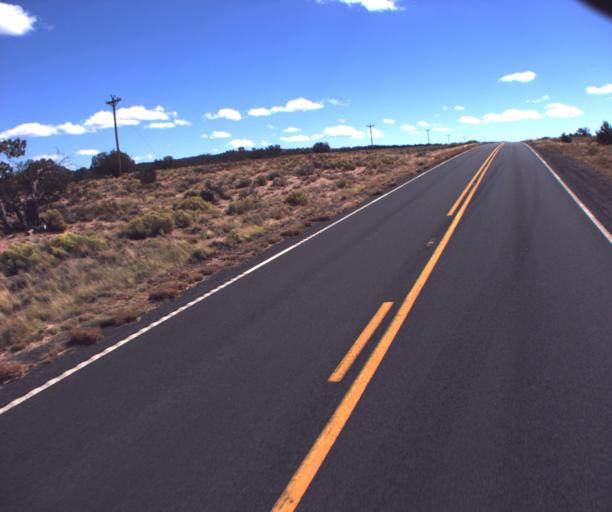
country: US
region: Arizona
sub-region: Apache County
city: Houck
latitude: 35.0830
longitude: -109.3066
